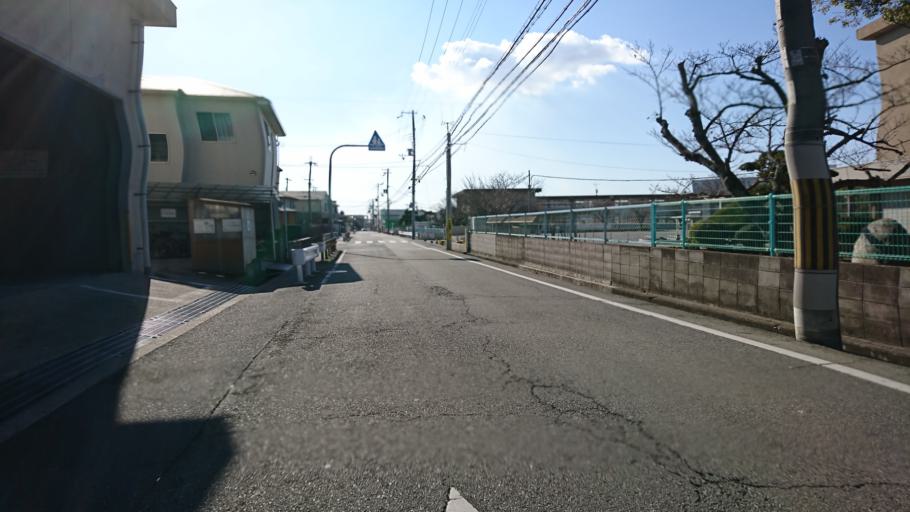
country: JP
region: Hyogo
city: Kakogawacho-honmachi
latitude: 34.7371
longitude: 134.8732
